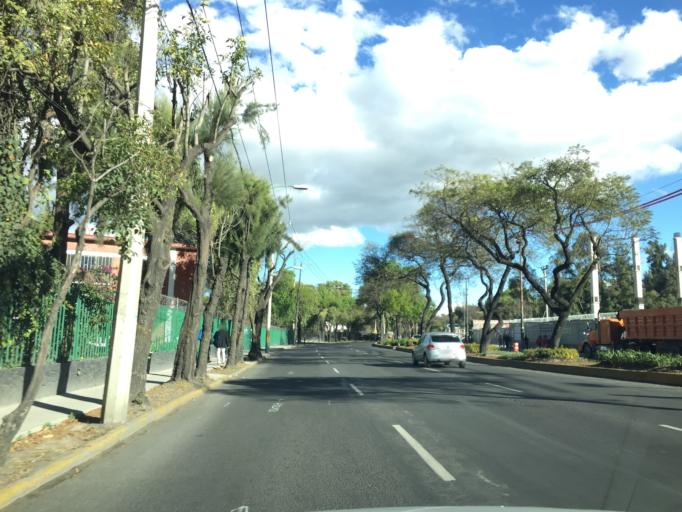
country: MX
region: Mexico
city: Colonia Lindavista
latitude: 19.4848
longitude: -99.1336
